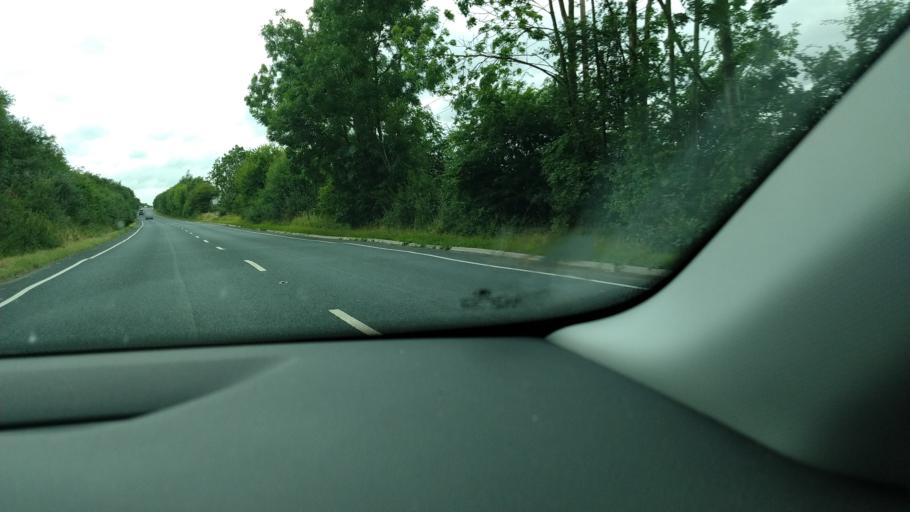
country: GB
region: England
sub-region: East Riding of Yorkshire
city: Rawcliffe
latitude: 53.7114
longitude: -0.9498
